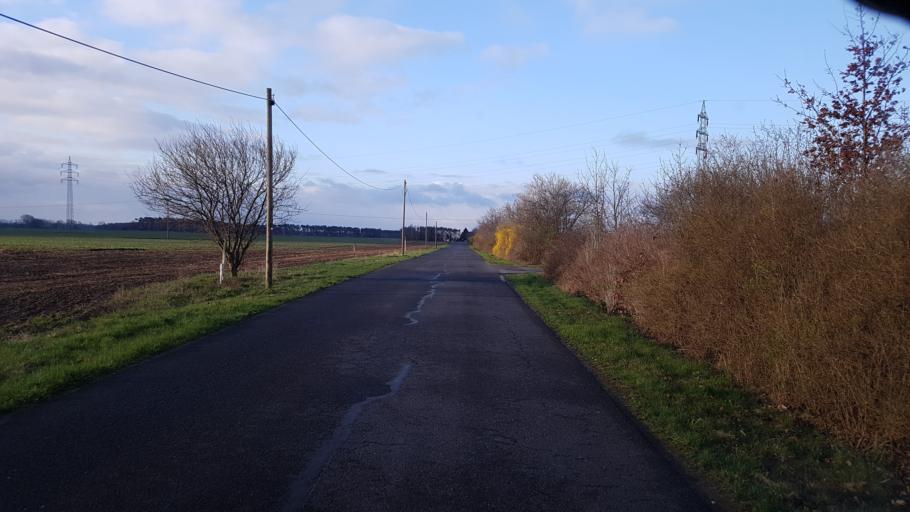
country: DE
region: Saxony
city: Nauwalde
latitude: 51.4533
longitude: 13.4215
